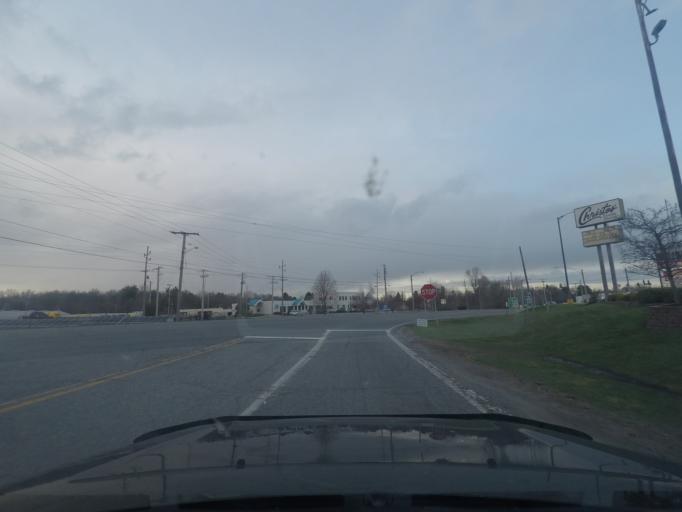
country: US
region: Indiana
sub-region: LaPorte County
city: LaPorte
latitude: 41.5993
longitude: -86.7391
